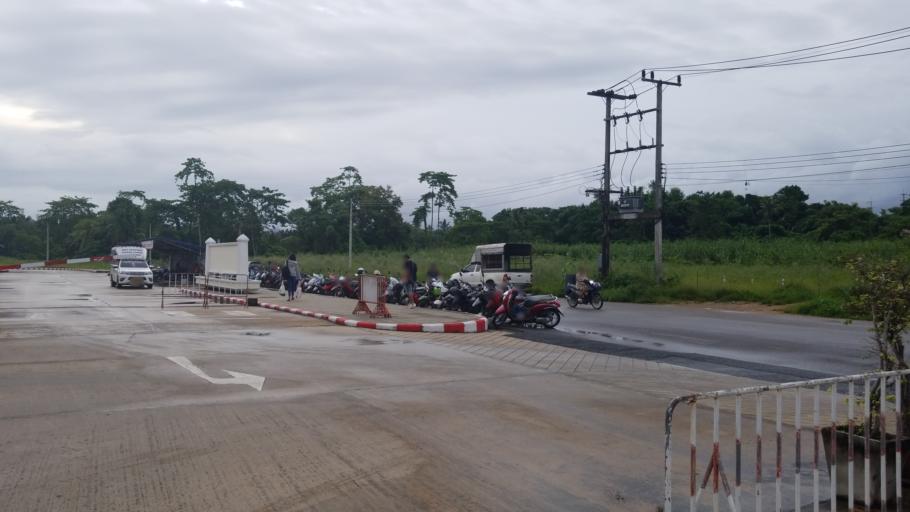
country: TH
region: Krabi
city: Krabi
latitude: 8.0997
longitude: 98.9063
